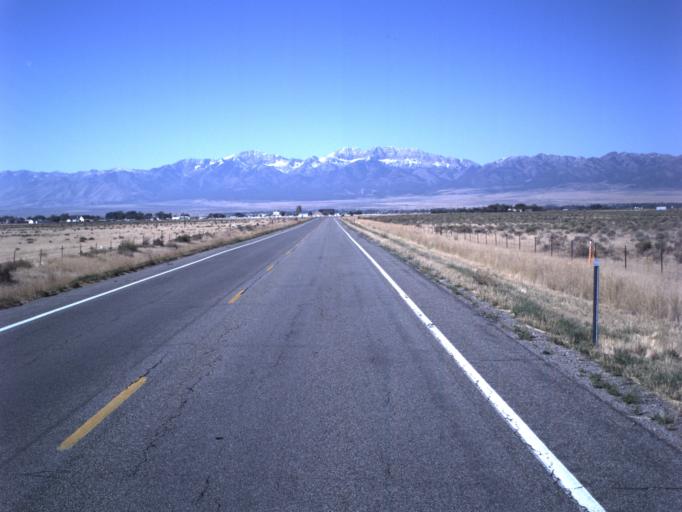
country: US
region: Utah
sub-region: Tooele County
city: Erda
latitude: 40.6097
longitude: -112.3803
